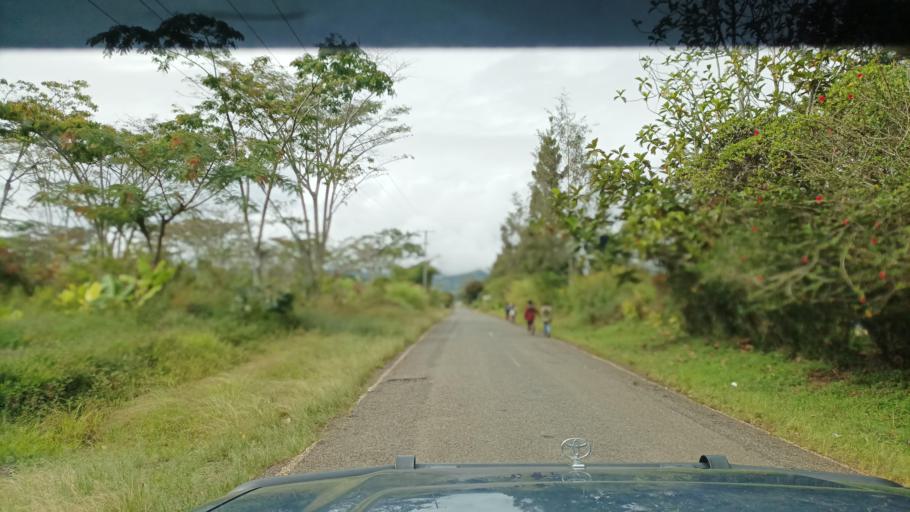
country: PG
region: Jiwaka
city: Minj
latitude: -5.8862
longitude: 144.6811
